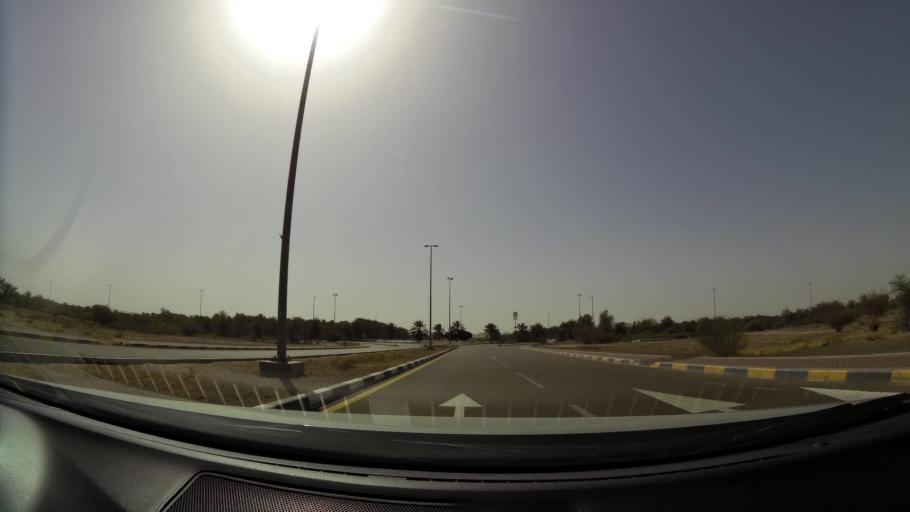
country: OM
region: Al Buraimi
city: Al Buraymi
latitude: 24.3159
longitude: 55.7953
